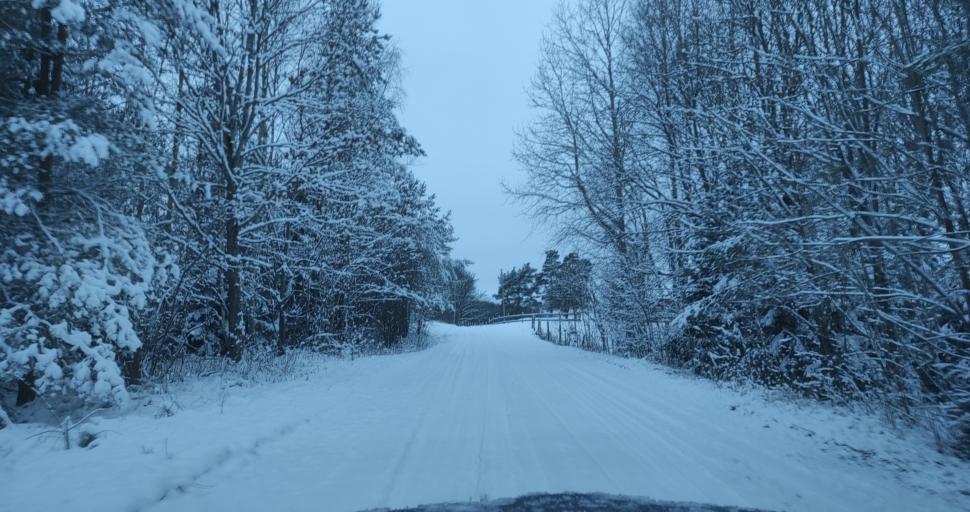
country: LV
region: Alsunga
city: Alsunga
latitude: 56.9576
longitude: 21.6119
